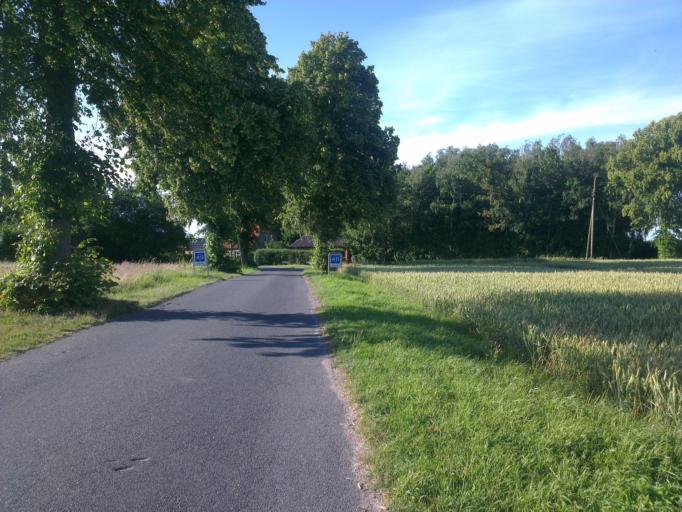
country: DK
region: Capital Region
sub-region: Frederikssund Kommune
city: Skibby
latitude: 55.7927
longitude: 11.9605
